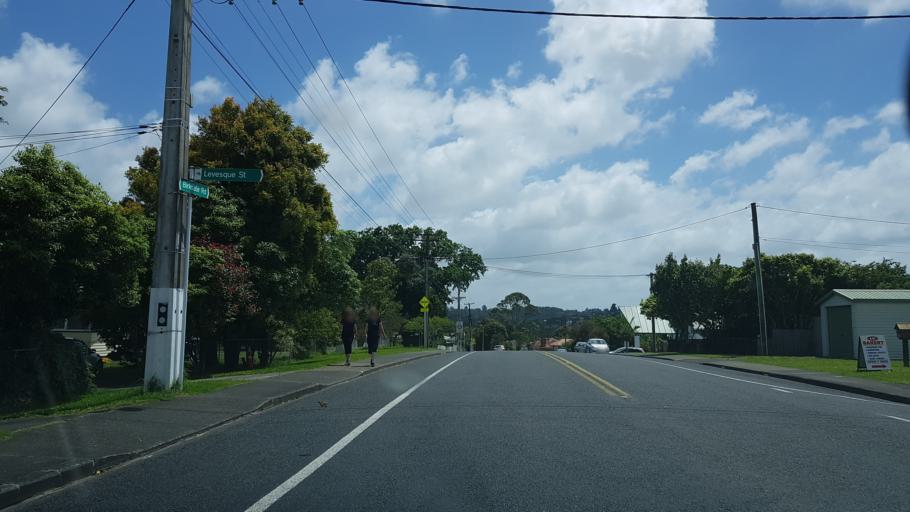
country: NZ
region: Auckland
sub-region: Auckland
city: North Shore
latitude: -36.7923
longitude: 174.7008
